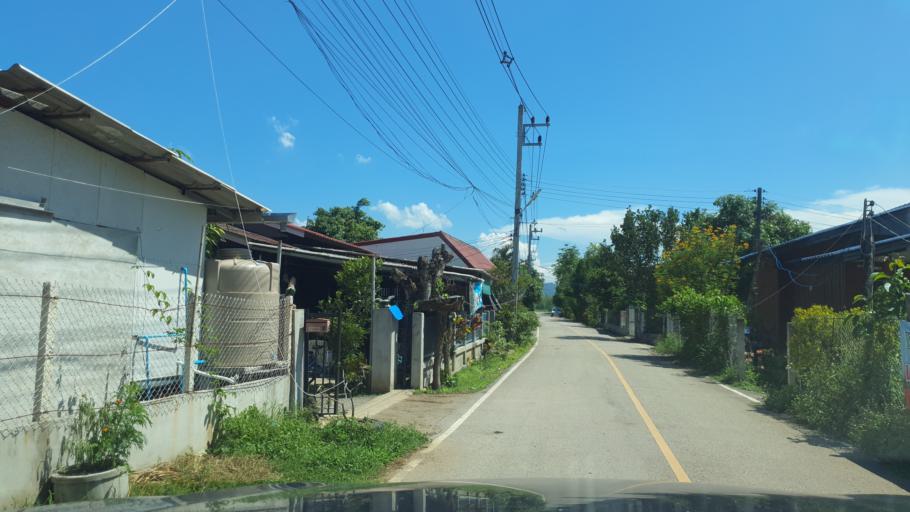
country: TH
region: Chiang Mai
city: Mae On
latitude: 18.7972
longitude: 99.2653
